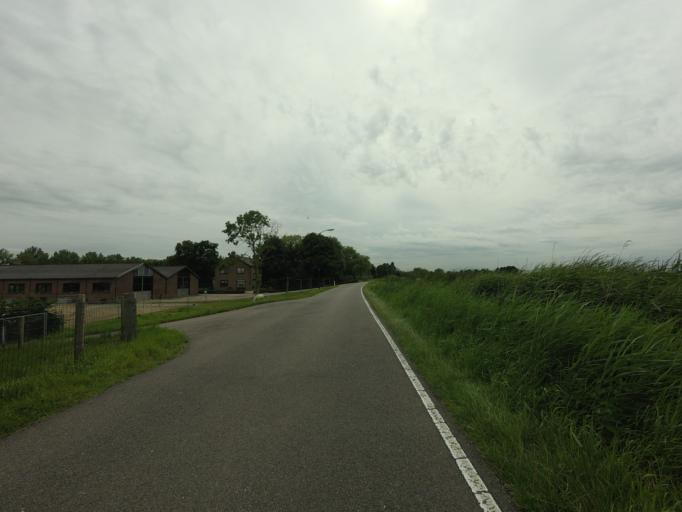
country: NL
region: North Holland
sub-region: Gemeente Uithoorn
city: Uithoorn
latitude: 52.2144
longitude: 4.8183
